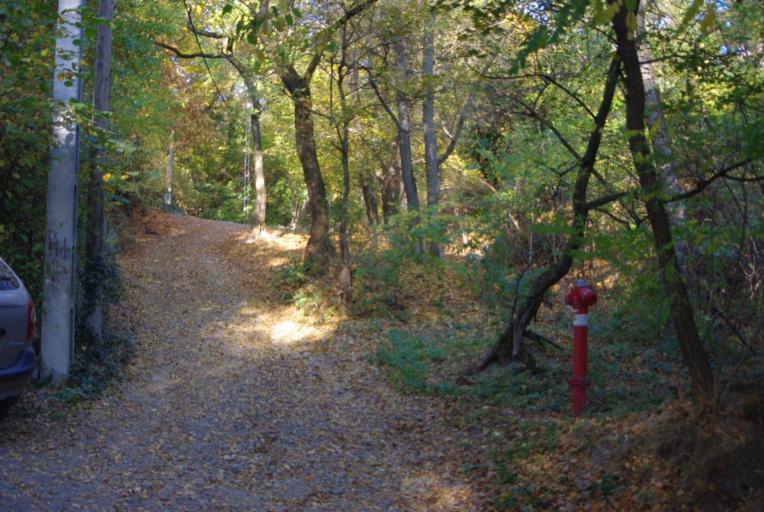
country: HU
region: Pest
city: Leanyfalu
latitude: 47.7182
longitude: 19.0780
